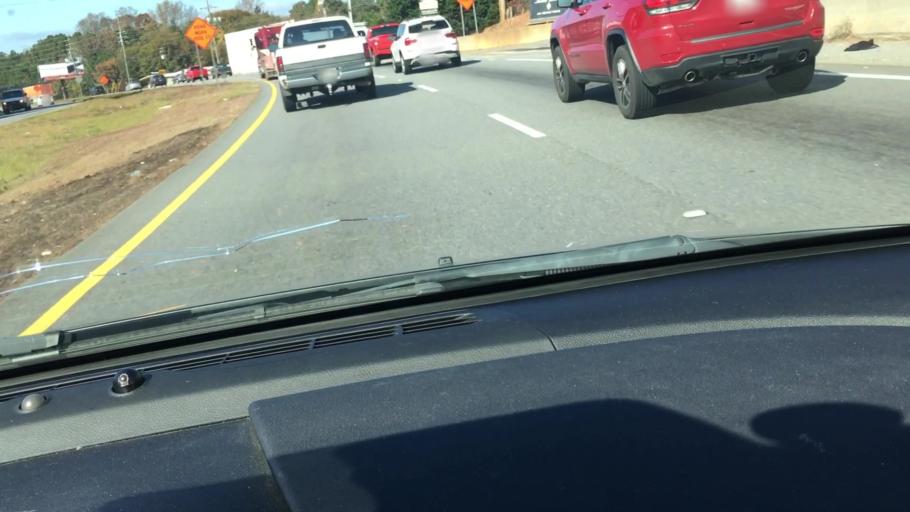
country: US
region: Georgia
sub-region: Fulton County
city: Milton
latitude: 34.1271
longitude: -84.2248
